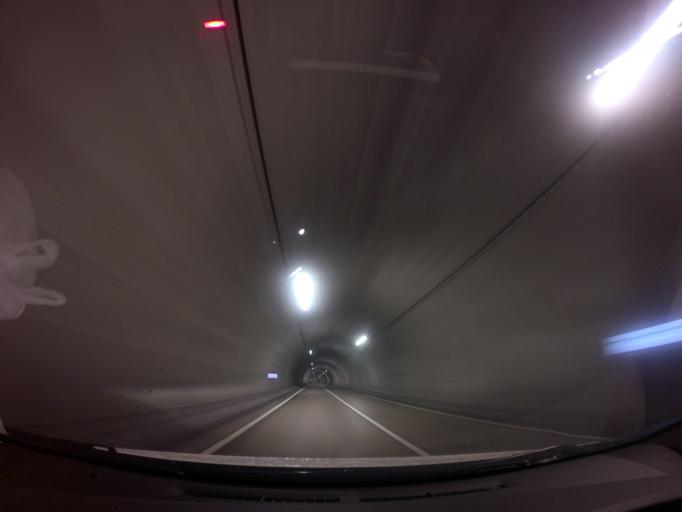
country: JP
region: Wakayama
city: Koya
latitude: 33.9784
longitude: 135.8076
